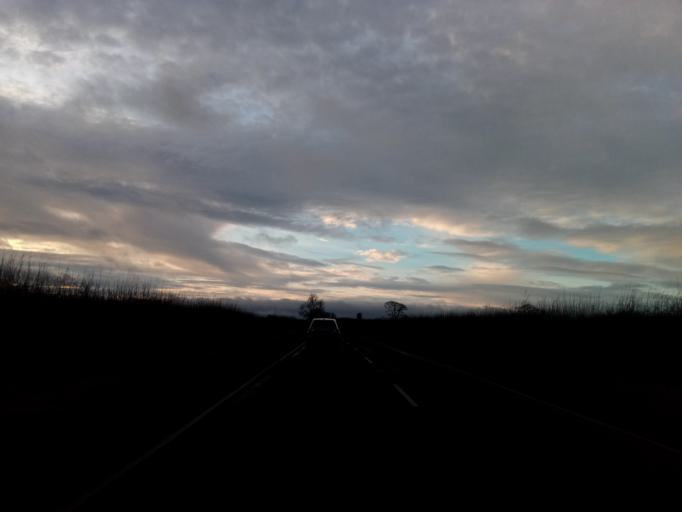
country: GB
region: England
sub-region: Northumberland
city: Ponteland
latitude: 55.0743
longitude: -1.7153
